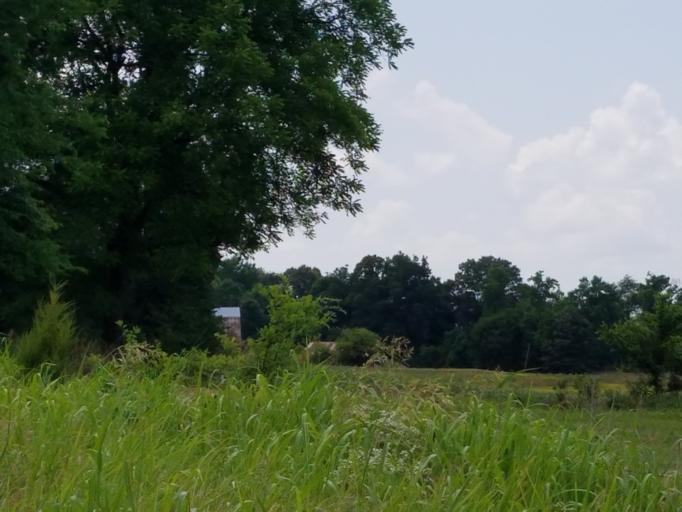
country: US
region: Tennessee
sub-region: Gibson County
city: Medina
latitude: 35.7725
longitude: -88.6692
